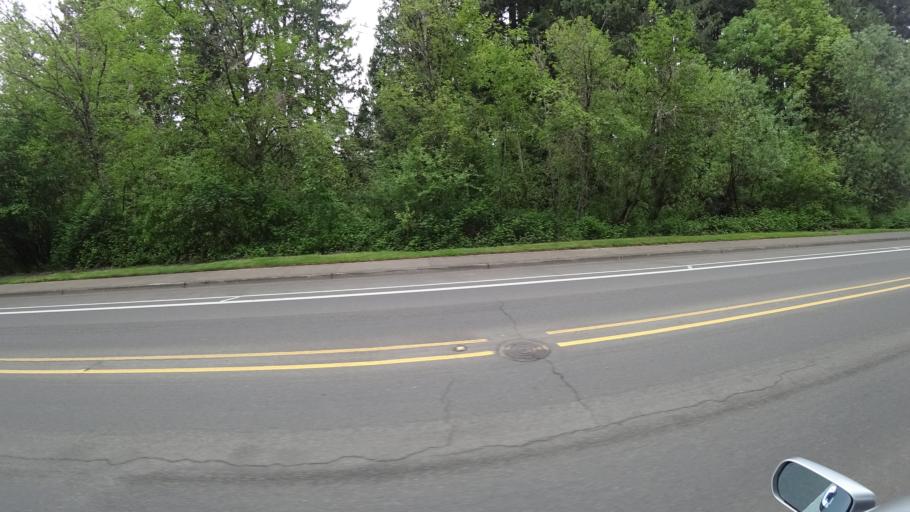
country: US
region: Oregon
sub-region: Washington County
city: Hillsboro
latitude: 45.5370
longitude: -122.9894
